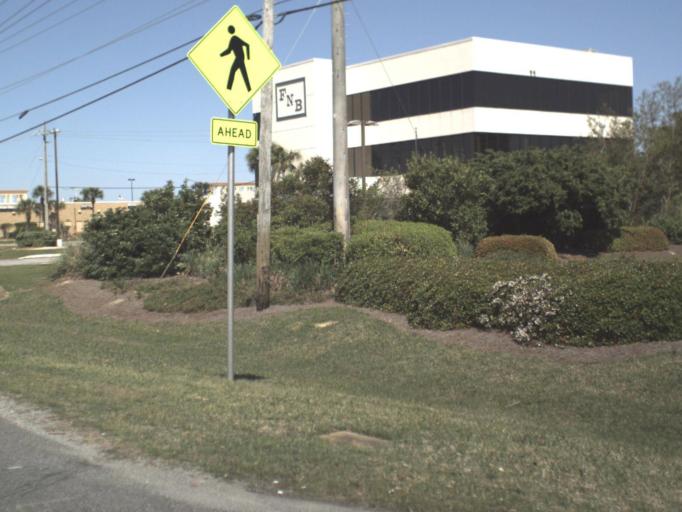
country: US
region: Florida
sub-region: Okaloosa County
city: Destin
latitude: 30.3872
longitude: -86.4461
